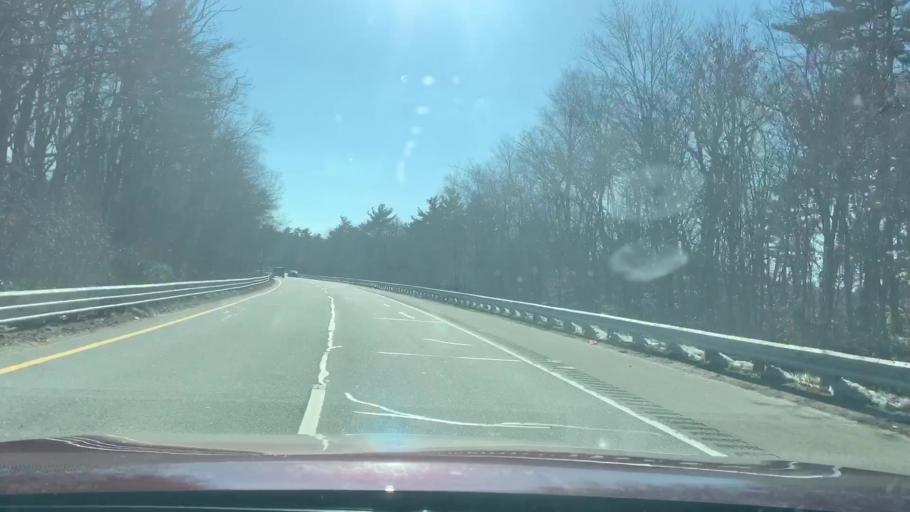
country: US
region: Massachusetts
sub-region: Essex County
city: Essex
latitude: 42.6109
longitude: -70.7356
